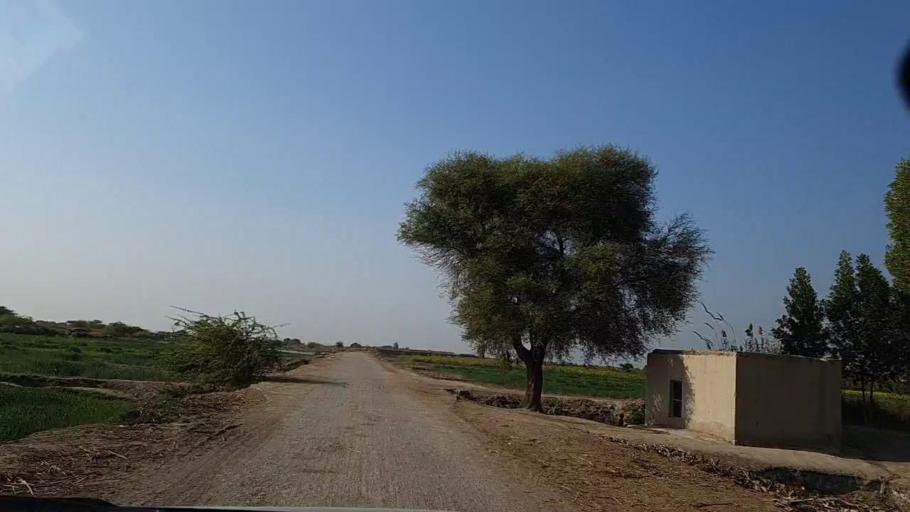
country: PK
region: Sindh
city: Mirwah Gorchani
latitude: 25.2286
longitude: 68.9838
